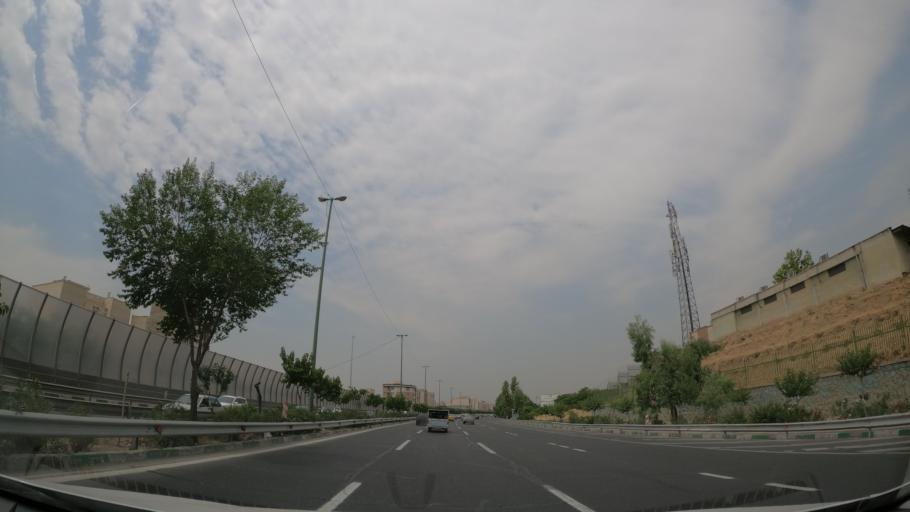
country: IR
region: Tehran
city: Tehran
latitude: 35.7389
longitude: 51.3639
